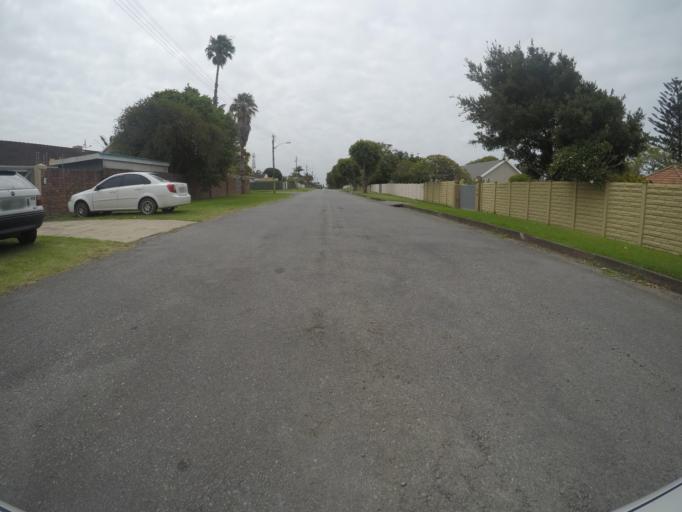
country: ZA
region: Eastern Cape
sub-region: Buffalo City Metropolitan Municipality
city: East London
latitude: -32.9733
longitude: 27.9400
